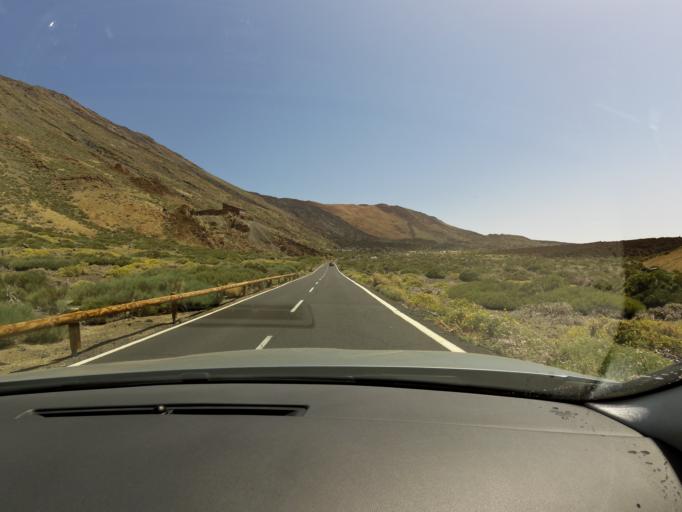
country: ES
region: Canary Islands
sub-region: Provincia de Santa Cruz de Tenerife
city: Vilaflor
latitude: 28.2510
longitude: -16.6267
